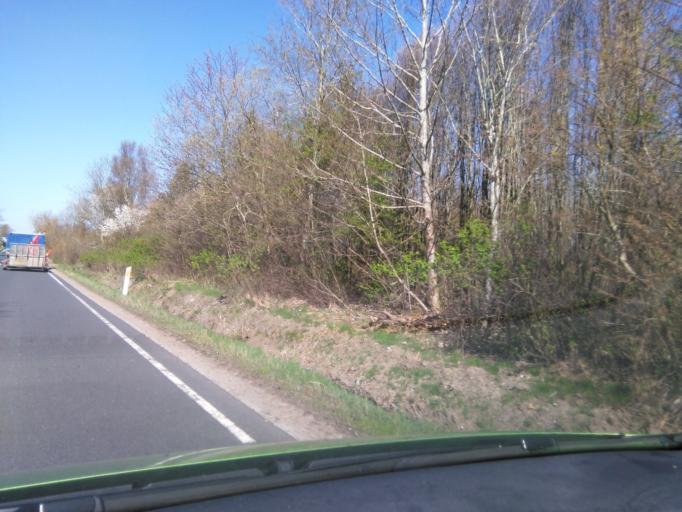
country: DK
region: South Denmark
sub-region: Billund Kommune
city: Grindsted
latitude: 55.7065
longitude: 8.7569
